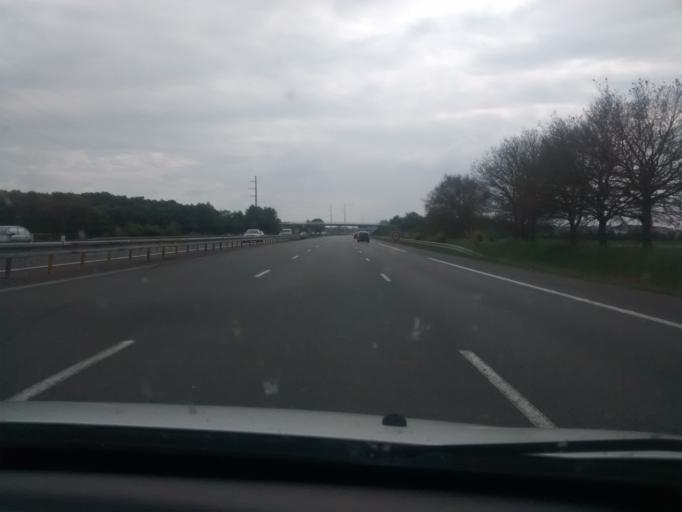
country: FR
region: Centre
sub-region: Departement d'Eure-et-Loir
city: Bailleau-le-Pin
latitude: 48.2961
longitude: 1.2820
